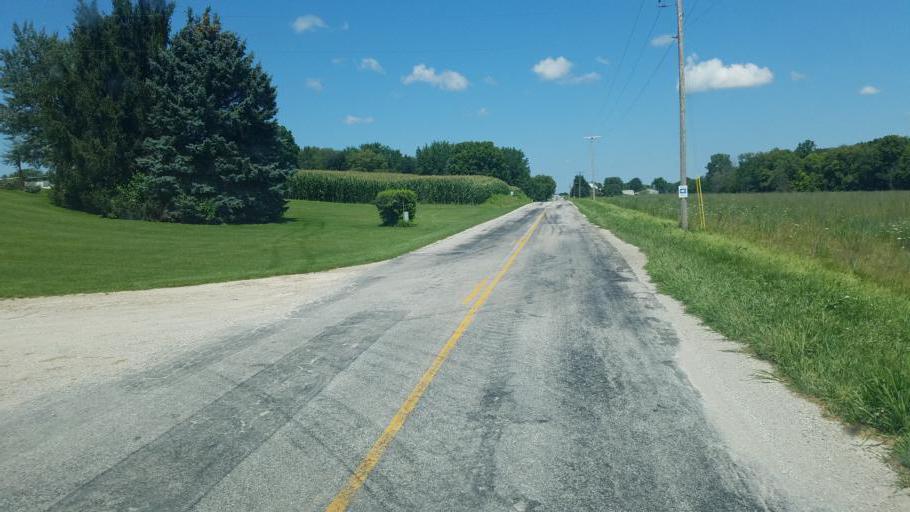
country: US
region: Ohio
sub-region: Marion County
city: Prospect
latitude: 40.5037
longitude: -83.2002
